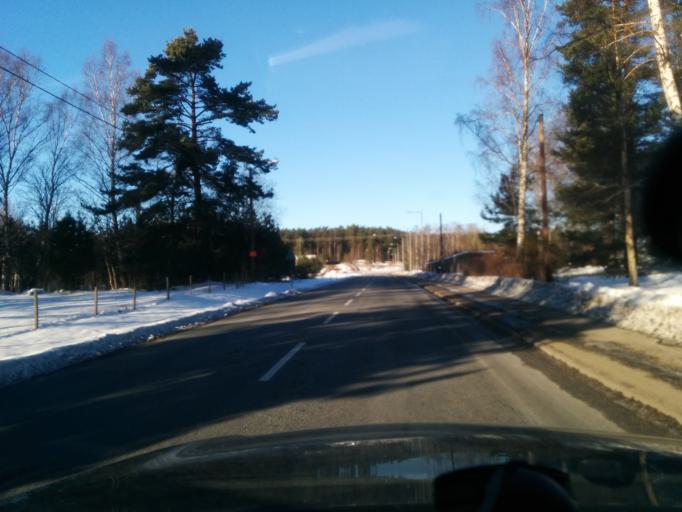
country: SE
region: Stockholm
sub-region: Taby Kommun
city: Taby
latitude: 59.4751
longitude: 18.0958
